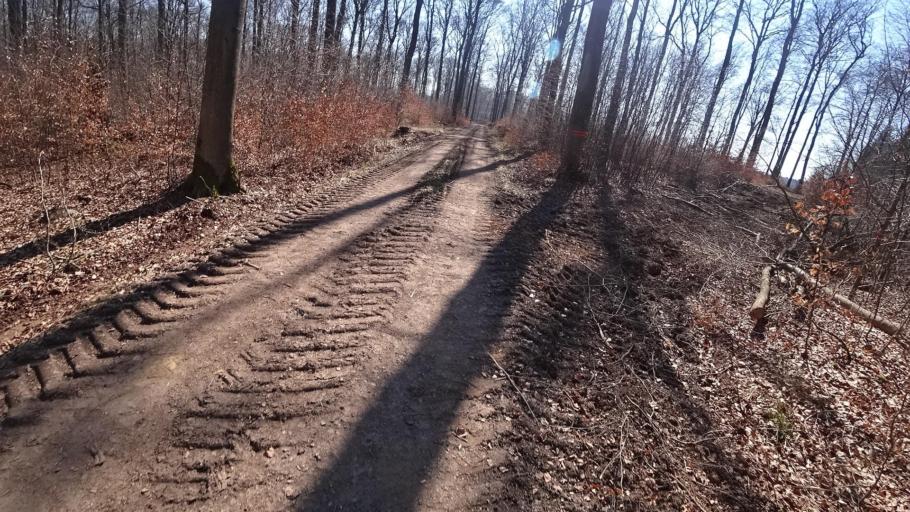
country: DE
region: Rheinland-Pfalz
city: Steinbach
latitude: 50.0342
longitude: 7.6083
